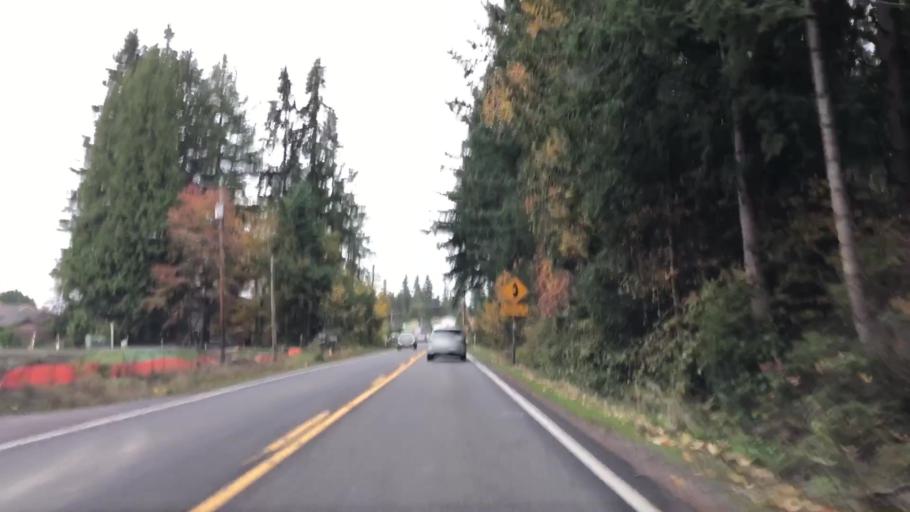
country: US
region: Washington
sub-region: Snohomish County
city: Martha Lake
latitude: 47.8198
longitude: -122.2321
